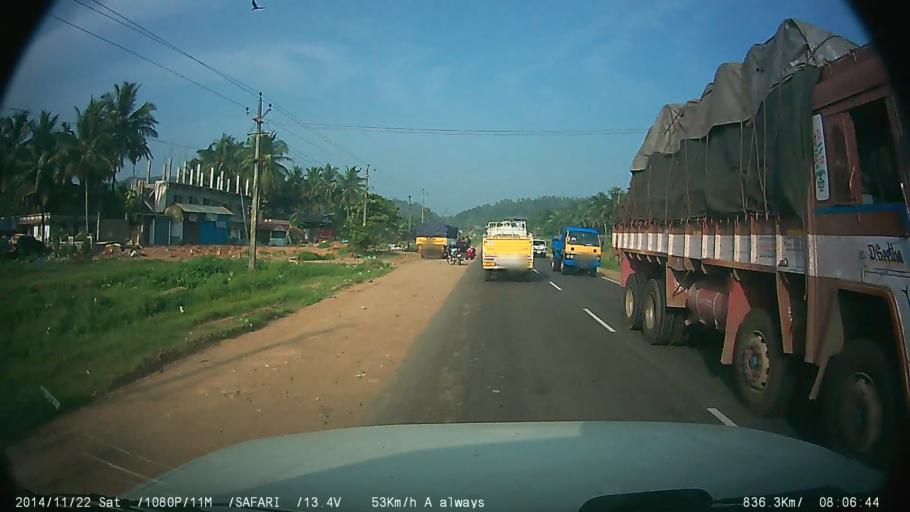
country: IN
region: Kerala
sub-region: Thrissur District
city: Chelakara
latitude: 10.5912
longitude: 76.4705
